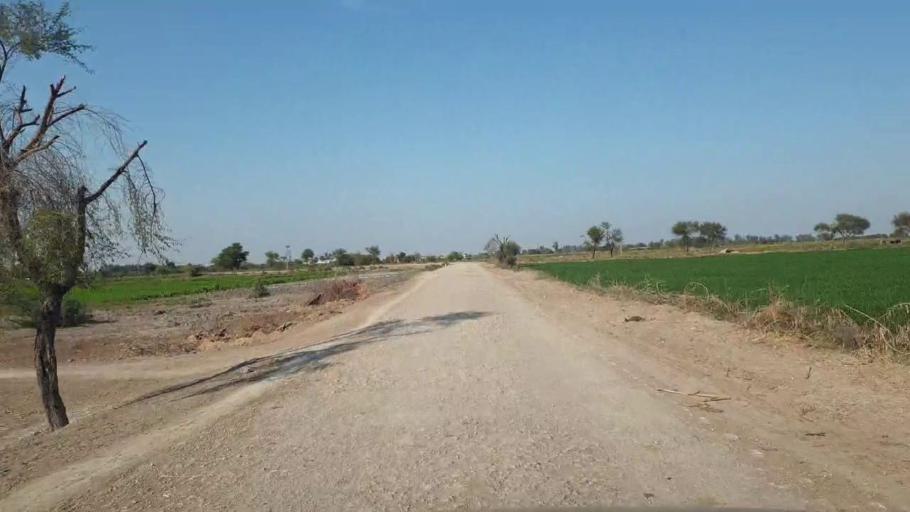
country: PK
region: Sindh
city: Shahpur Chakar
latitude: 26.1673
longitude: 68.6819
